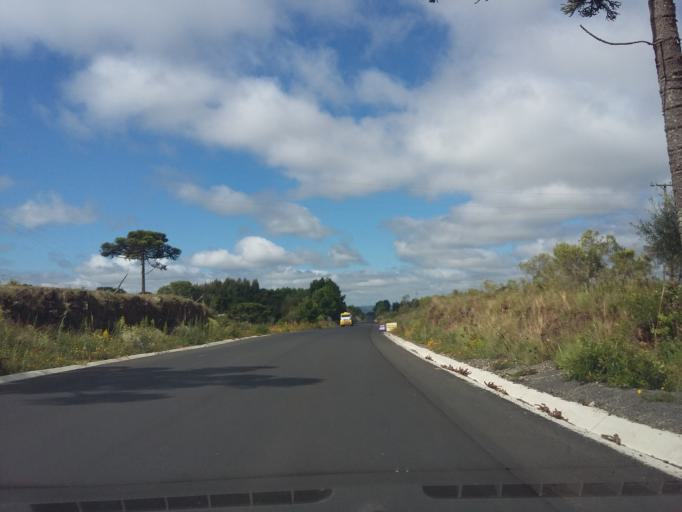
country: BR
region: Santa Catarina
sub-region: Sao Joaquim
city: Sao Joaquim
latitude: -28.0434
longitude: -50.0726
